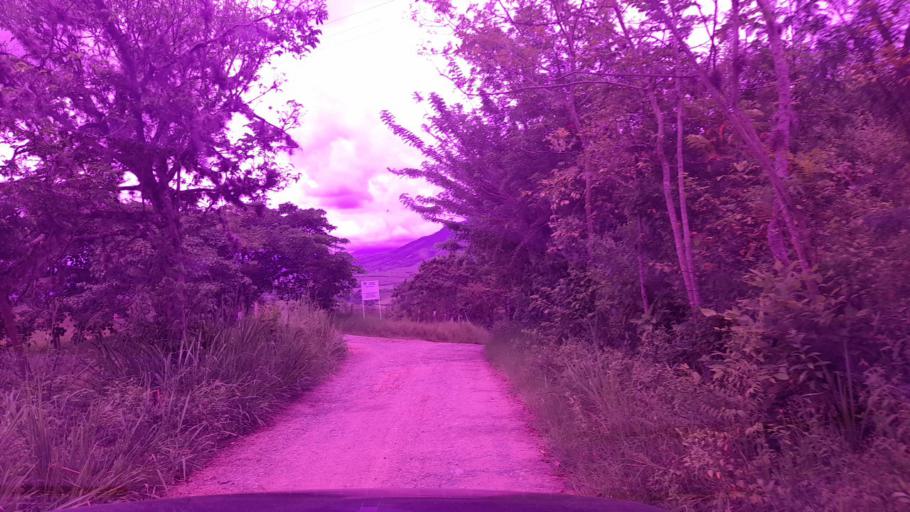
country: CO
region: Valle del Cauca
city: Andalucia
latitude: 4.1722
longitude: -76.1010
